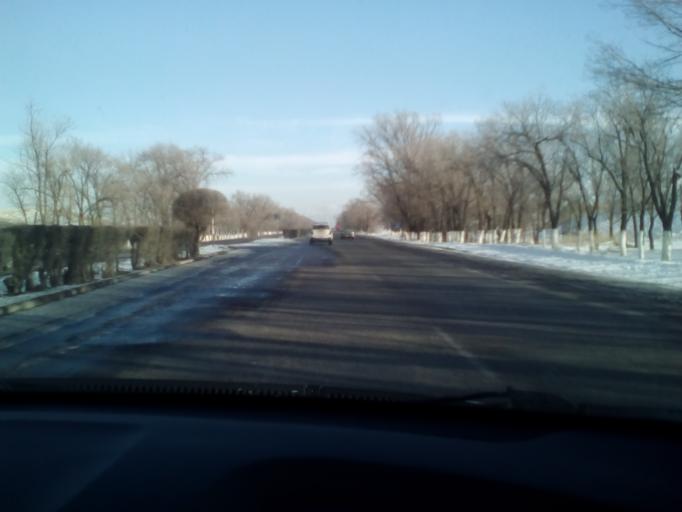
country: KZ
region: Almaty Oblysy
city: Burunday
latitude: 43.2222
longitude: 76.4305
